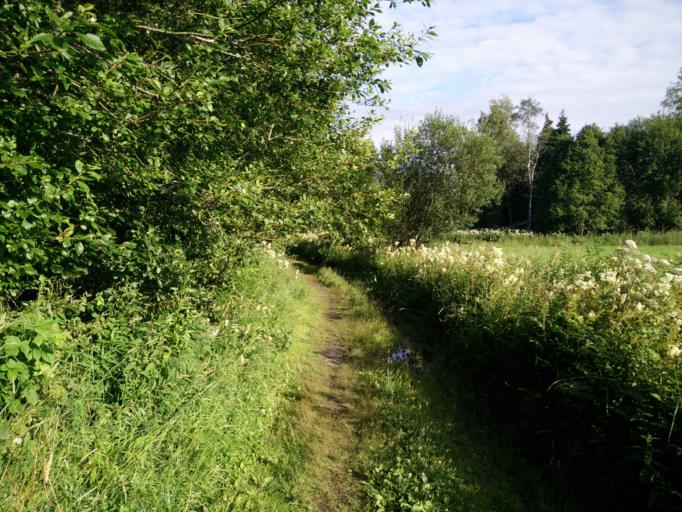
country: SE
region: Vaesternorrland
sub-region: Timra Kommun
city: Soraker
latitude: 62.4537
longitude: 17.4767
